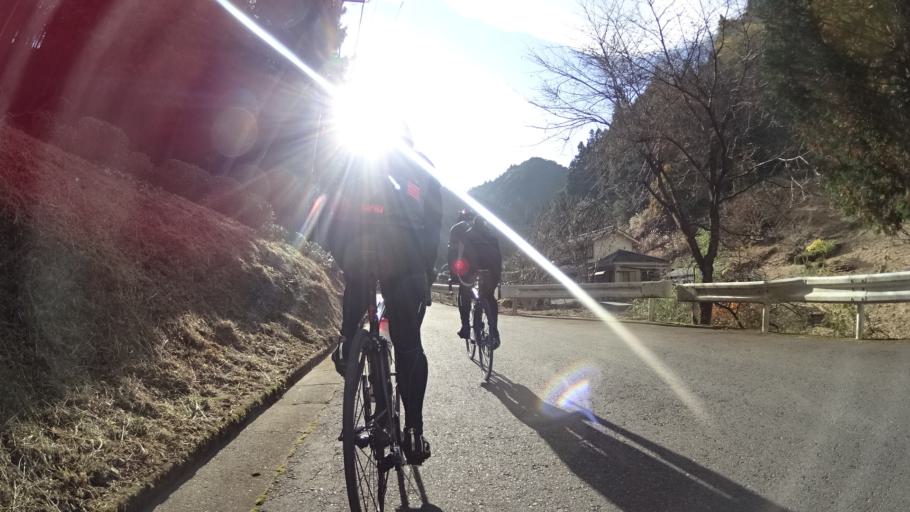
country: JP
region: Saitama
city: Chichibu
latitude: 35.9178
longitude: 139.1773
